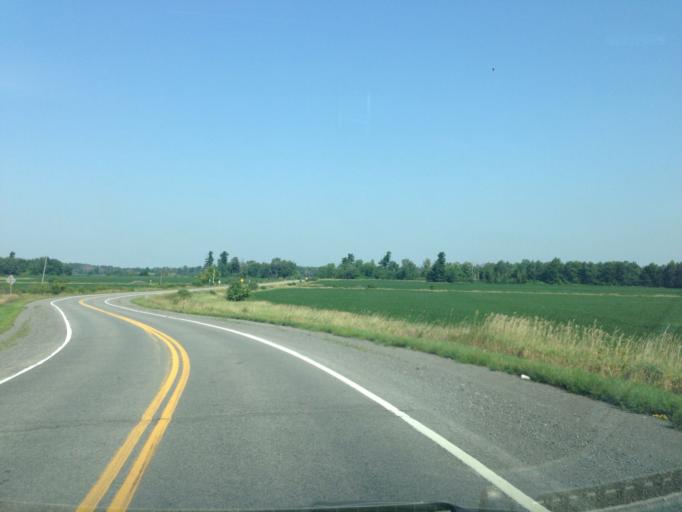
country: CA
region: Ontario
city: Ottawa
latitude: 45.3770
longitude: -75.5425
